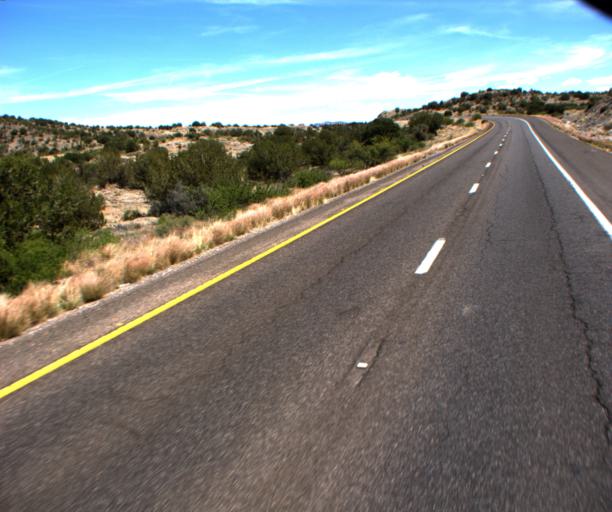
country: US
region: Arizona
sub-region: Yavapai County
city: Cornville
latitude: 34.7987
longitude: -111.9130
